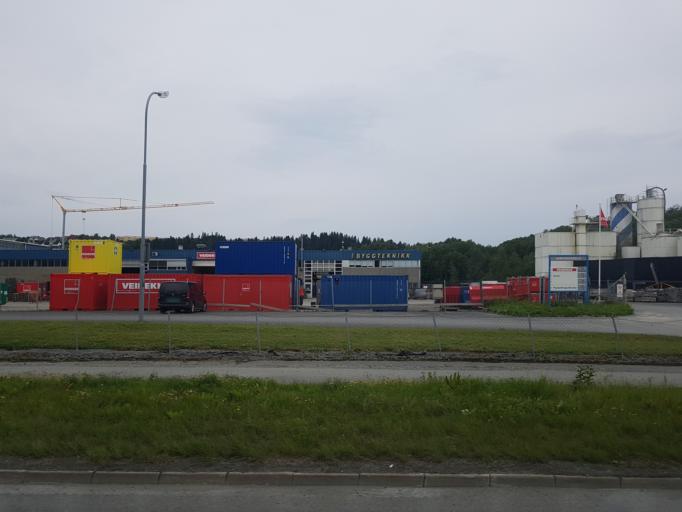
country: NO
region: Sor-Trondelag
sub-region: Trondheim
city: Trondheim
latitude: 63.3916
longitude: 10.3980
